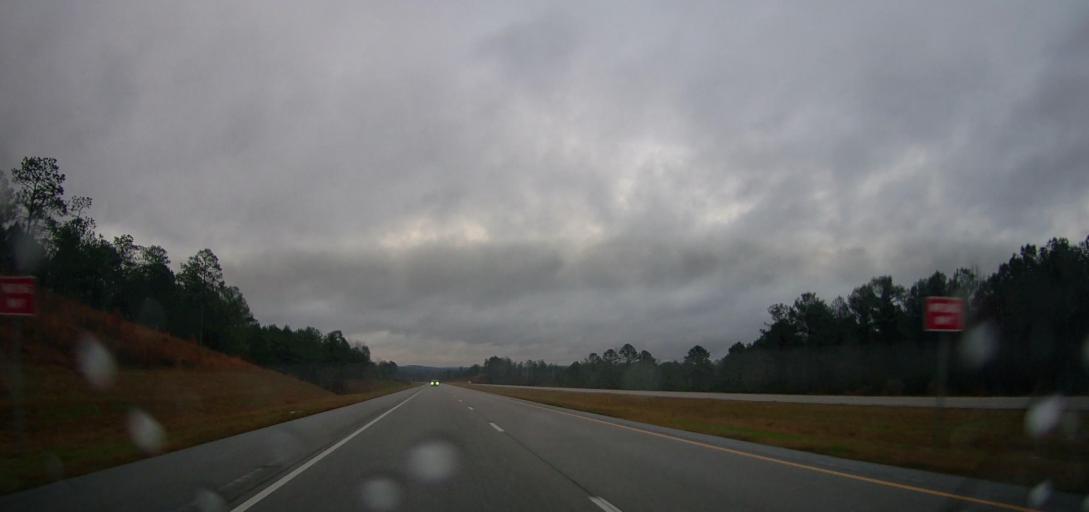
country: US
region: Alabama
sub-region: Bibb County
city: Centreville
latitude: 32.9504
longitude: -87.1050
